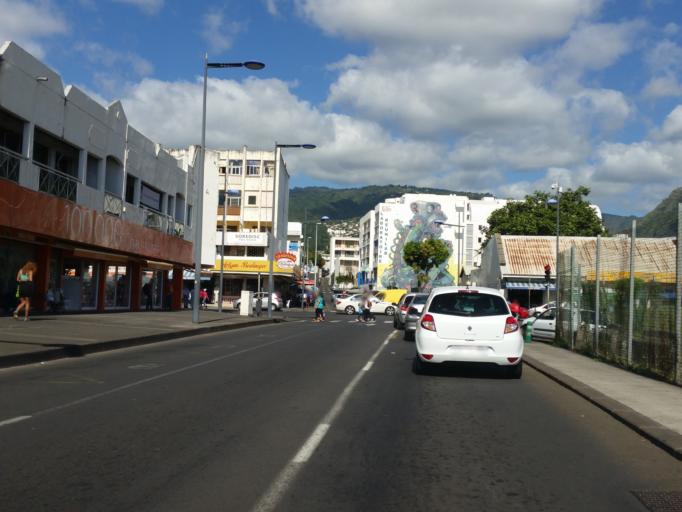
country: RE
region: Reunion
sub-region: Reunion
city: Saint-Denis
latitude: -20.8799
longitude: 55.4576
